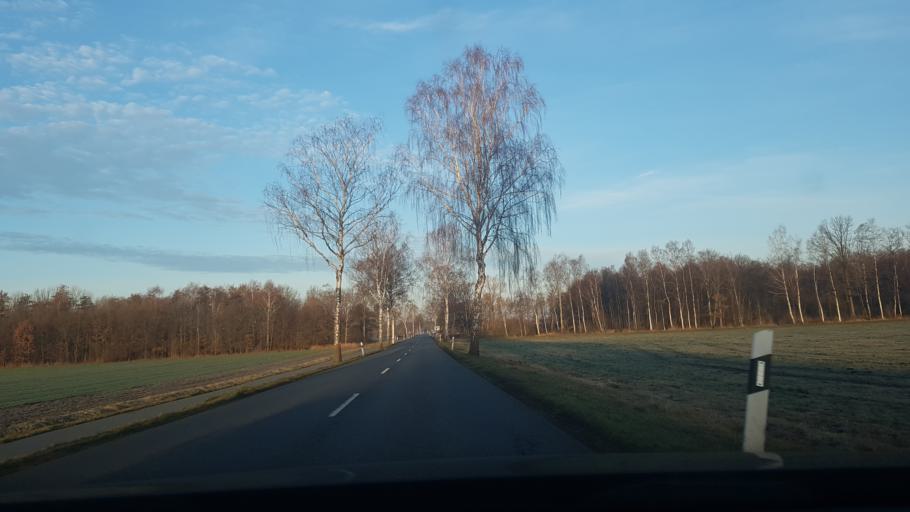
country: DE
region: Lower Saxony
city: Sassenburg
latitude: 52.5042
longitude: 10.6068
